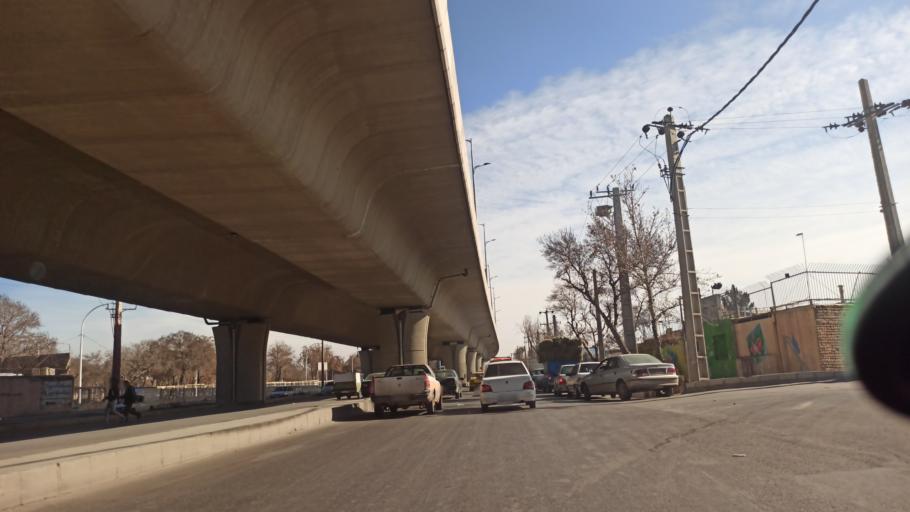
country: IR
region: Qazvin
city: Qazvin
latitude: 36.2561
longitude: 49.9964
